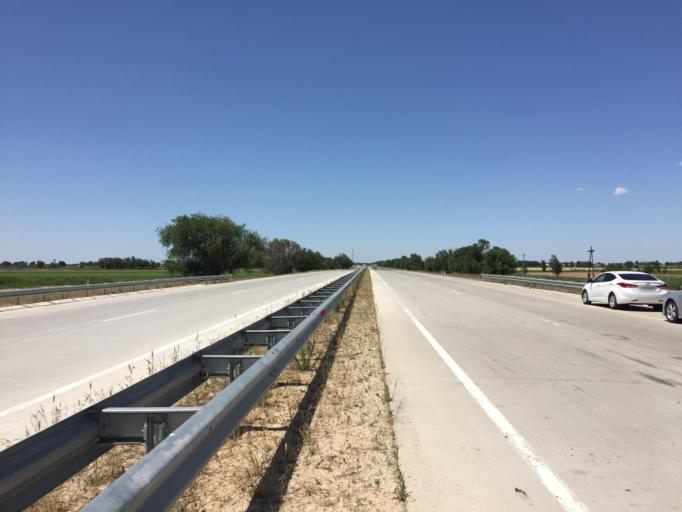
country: KZ
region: Ongtustik Qazaqstan
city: Shayan
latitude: 42.9111
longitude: 68.9784
